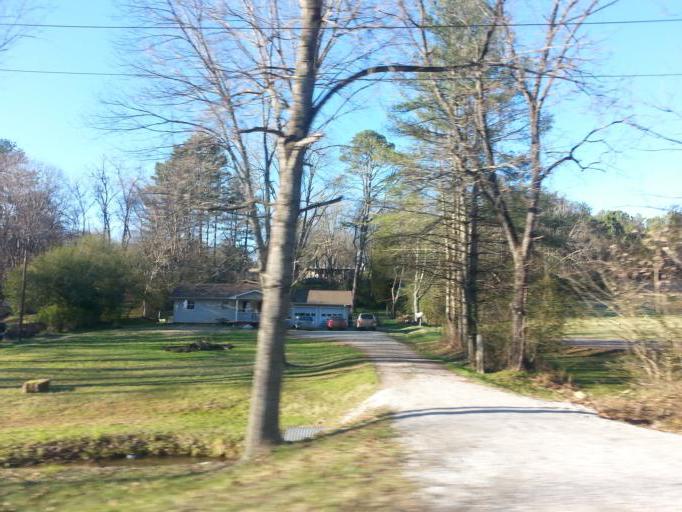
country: US
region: Tennessee
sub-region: Anderson County
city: Oak Ridge
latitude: 36.0633
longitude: -84.2230
